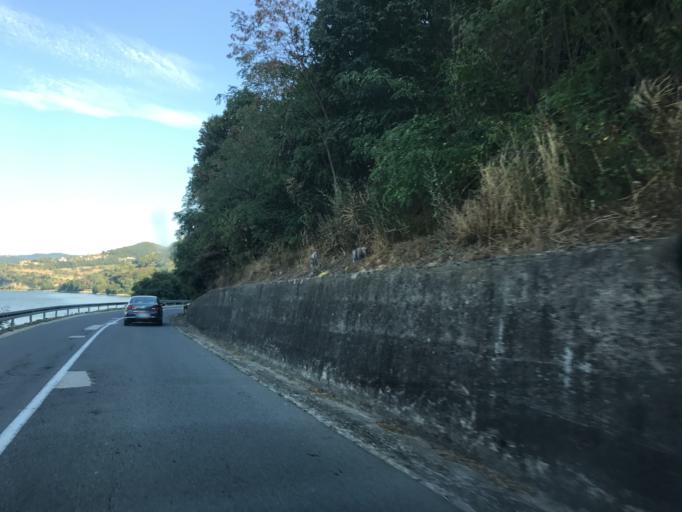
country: RO
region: Mehedinti
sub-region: Comuna Svinita
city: Svinita
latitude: 44.4701
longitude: 22.1207
